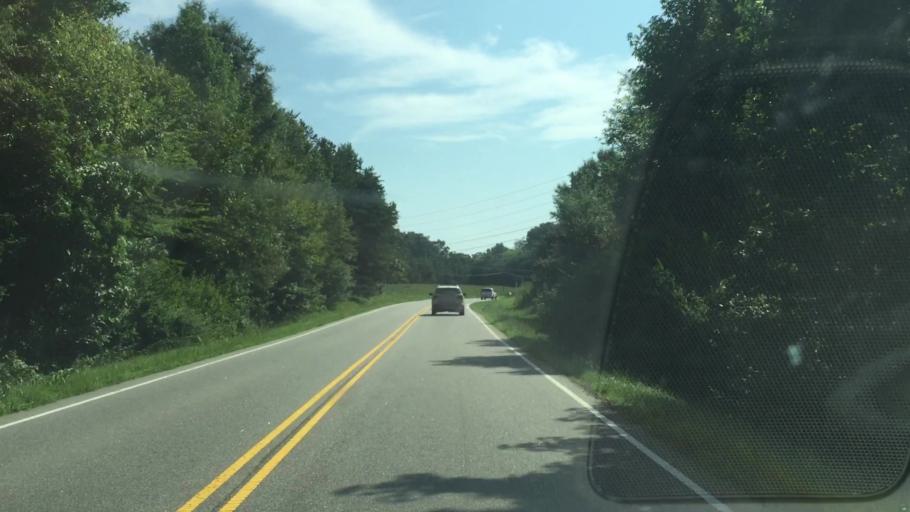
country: US
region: North Carolina
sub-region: Union County
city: Unionville
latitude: 35.1328
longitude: -80.4666
